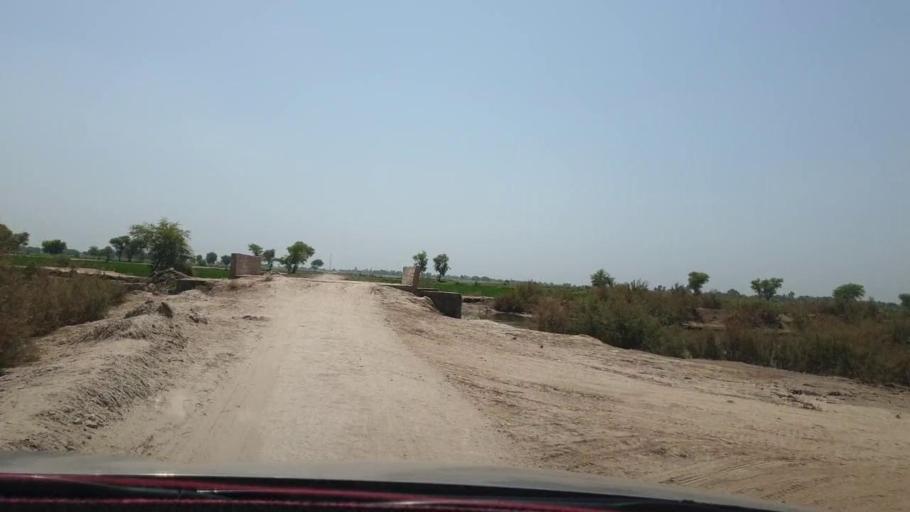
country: PK
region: Sindh
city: Kambar
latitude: 27.5667
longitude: 67.8816
